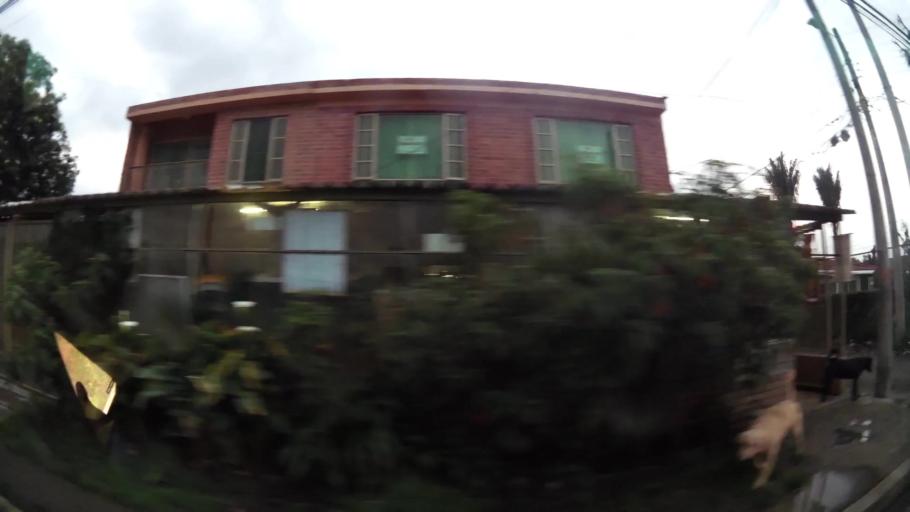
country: CO
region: Cundinamarca
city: Chia
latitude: 4.8419
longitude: -74.0592
